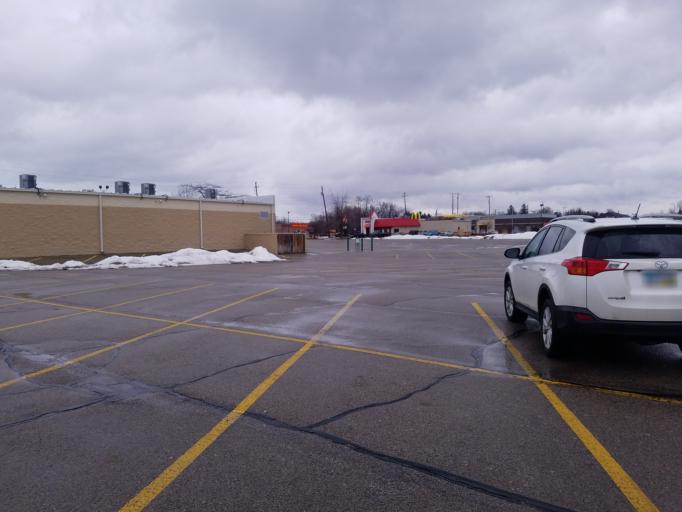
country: US
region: Ohio
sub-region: Lake County
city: North Madison
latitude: 41.8017
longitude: -81.0533
